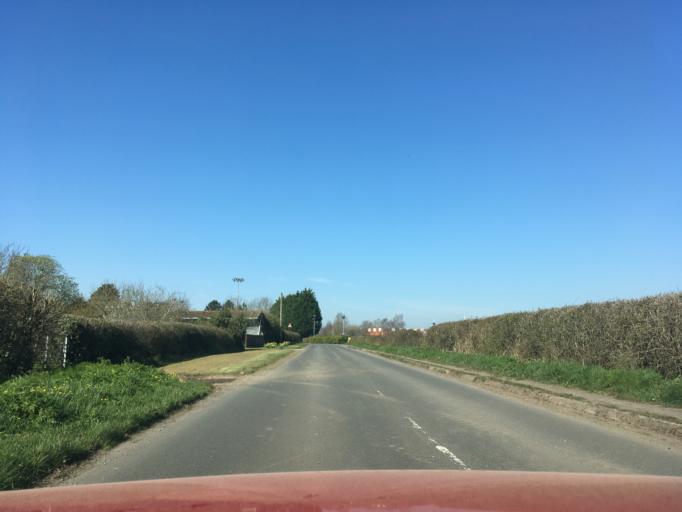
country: GB
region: England
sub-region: Gloucestershire
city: Berkeley
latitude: 51.6922
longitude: -2.4862
